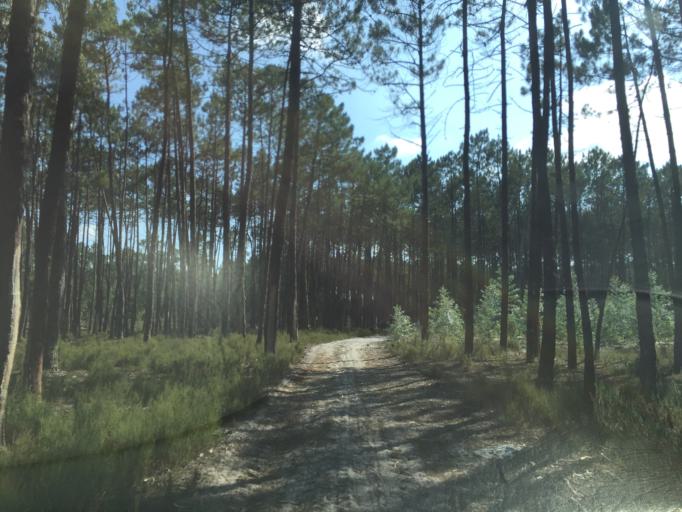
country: PT
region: Leiria
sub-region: Leiria
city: Monte Redondo
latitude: 39.9550
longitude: -8.8220
